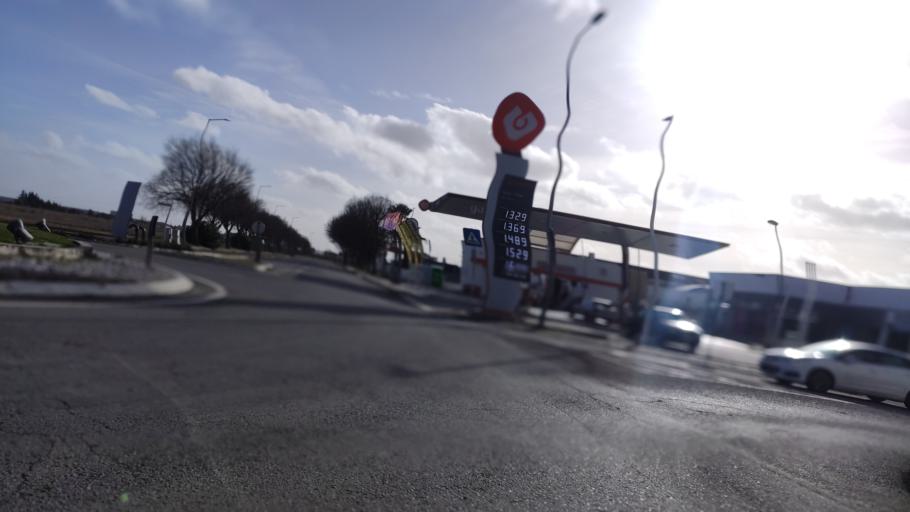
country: PT
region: Beja
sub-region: Beja
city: Beja
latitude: 38.0058
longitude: -7.8654
